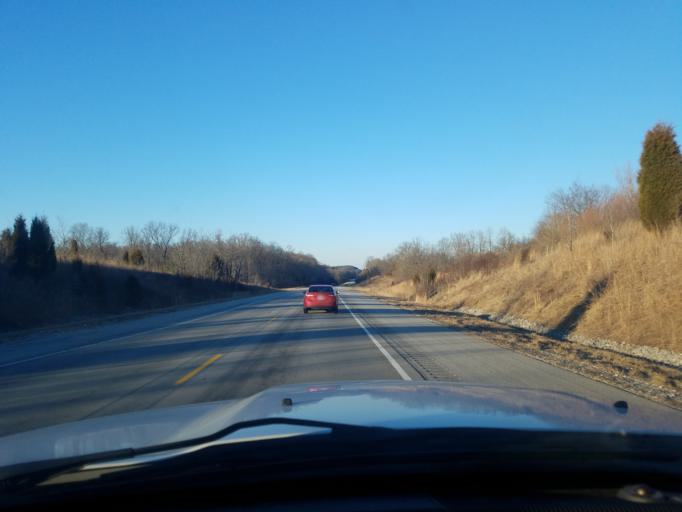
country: US
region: Indiana
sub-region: Crawford County
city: English
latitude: 38.1755
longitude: -86.6042
